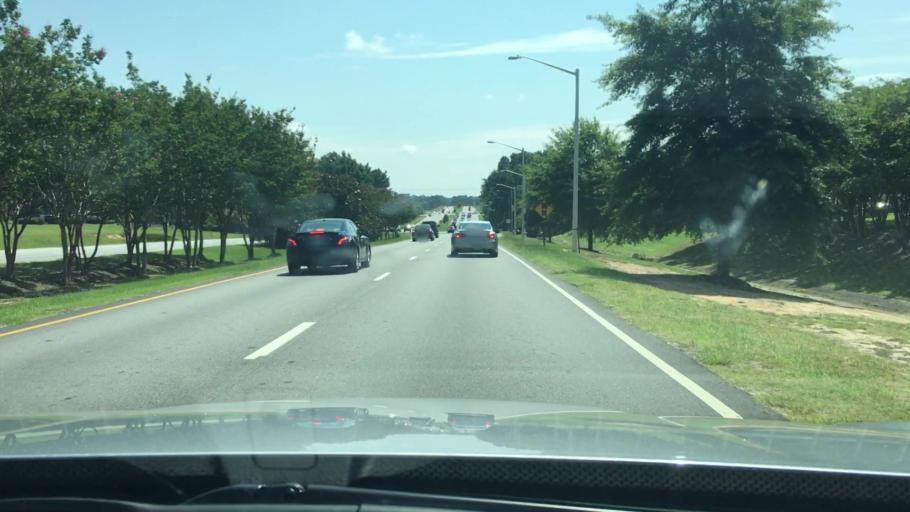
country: US
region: South Carolina
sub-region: Florence County
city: Florence
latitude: 34.1889
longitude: -79.8316
